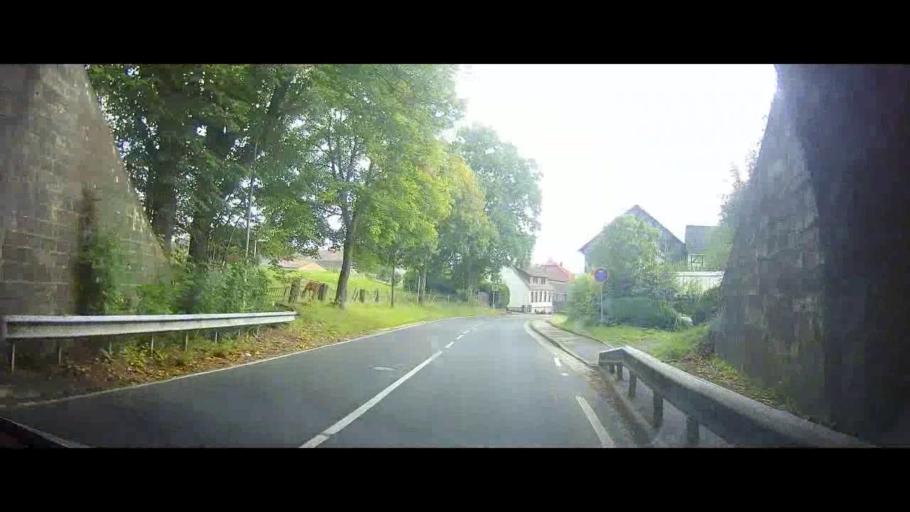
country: DE
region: Lower Saxony
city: Uslar
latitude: 51.6526
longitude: 9.6494
